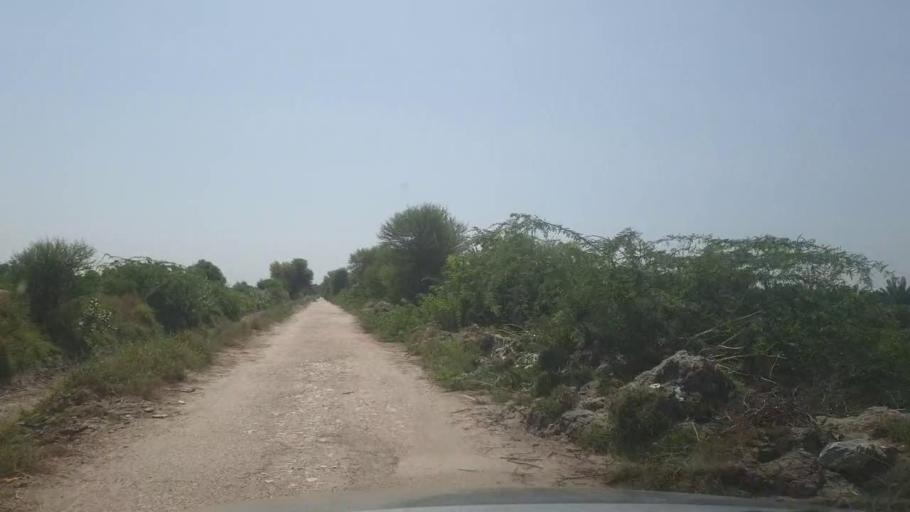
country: PK
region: Sindh
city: Khairpur
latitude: 27.3650
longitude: 69.0243
